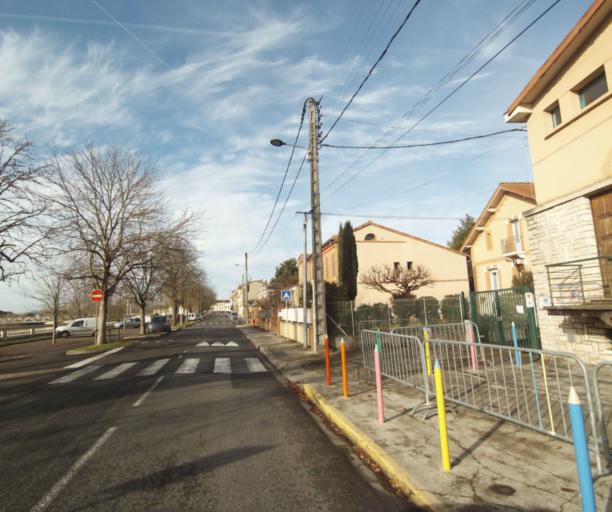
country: FR
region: Midi-Pyrenees
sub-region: Departement de la Haute-Garonne
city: Villemur-sur-Tarn
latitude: 43.8614
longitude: 1.5078
